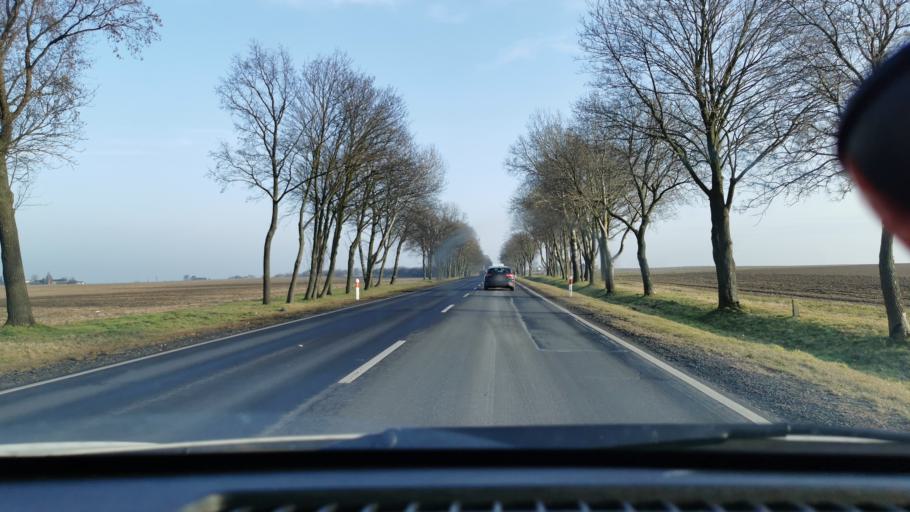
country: PL
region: Lodz Voivodeship
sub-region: Powiat sieradzki
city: Wroblew
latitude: 51.6201
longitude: 18.5869
